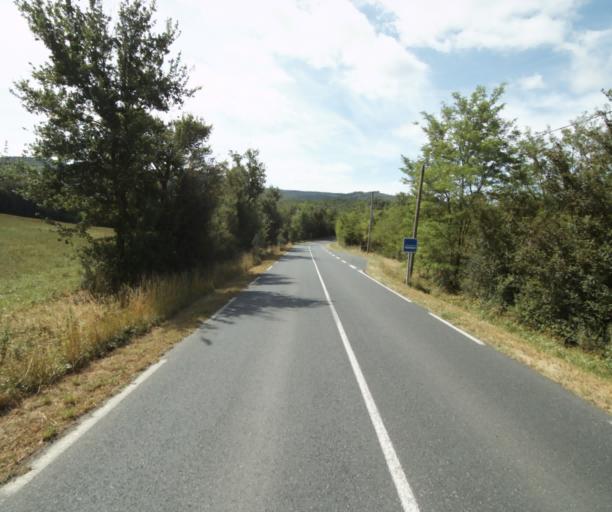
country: FR
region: Midi-Pyrenees
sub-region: Departement du Tarn
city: Dourgne
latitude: 43.4774
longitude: 2.1092
